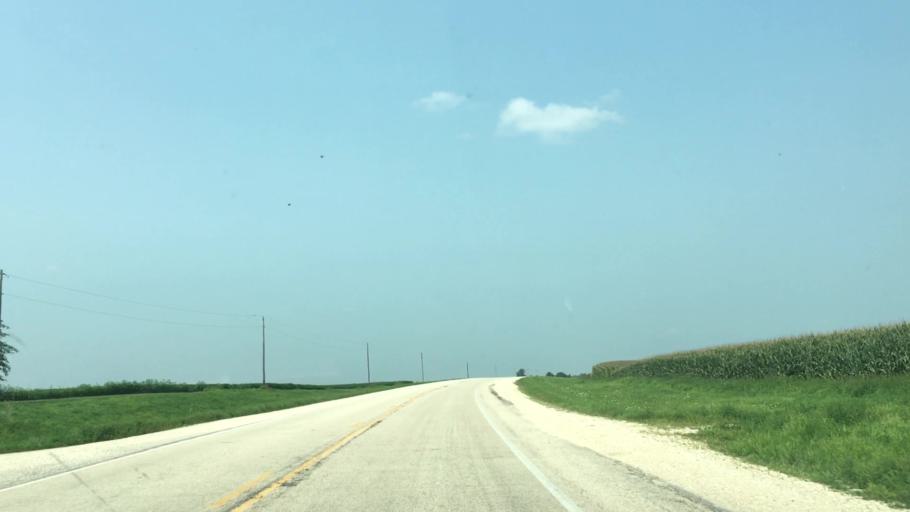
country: US
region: Iowa
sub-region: Fayette County
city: West Union
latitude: 42.9812
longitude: -91.8242
